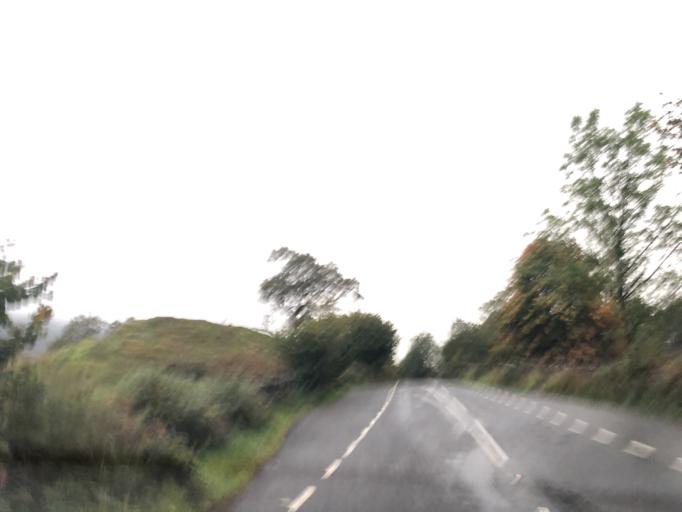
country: GB
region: England
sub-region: Cumbria
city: Windermere
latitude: 54.4347
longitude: -2.9020
